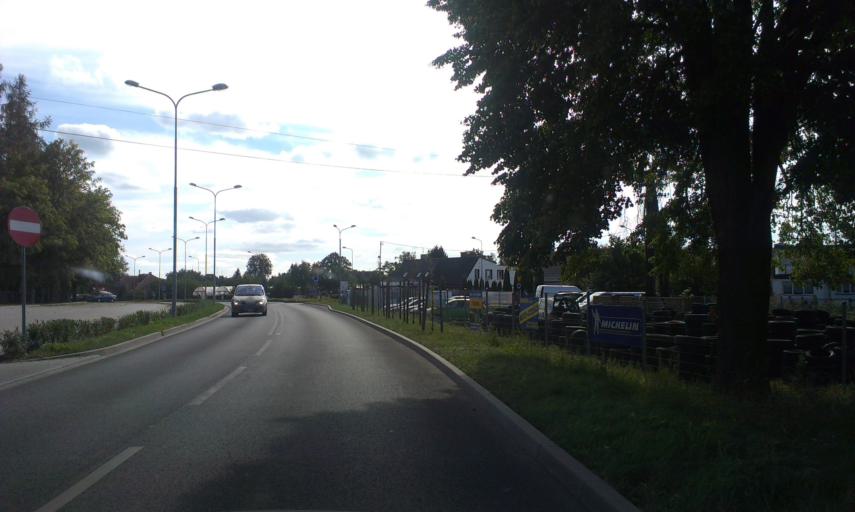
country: PL
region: Greater Poland Voivodeship
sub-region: Powiat zlotowski
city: Zlotow
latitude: 53.3704
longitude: 17.0225
